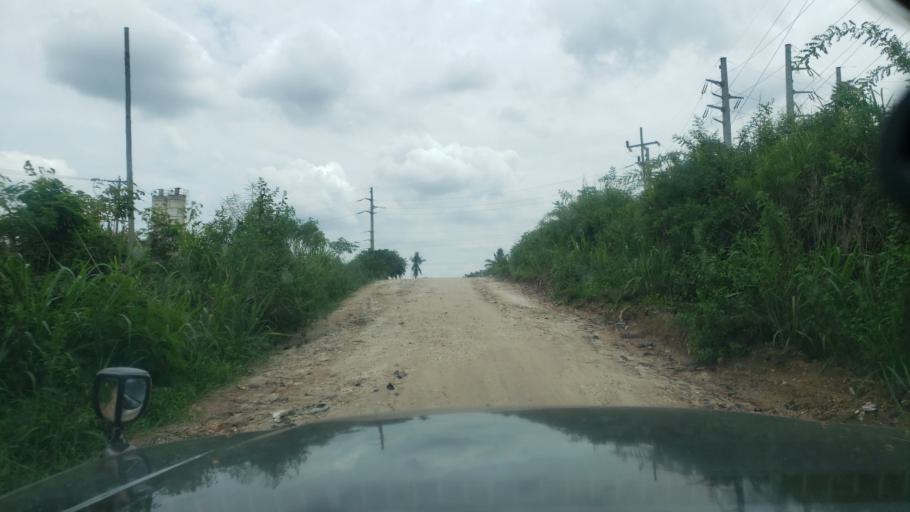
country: TZ
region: Pwani
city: Kisarawe
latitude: -6.8825
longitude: 39.1500
